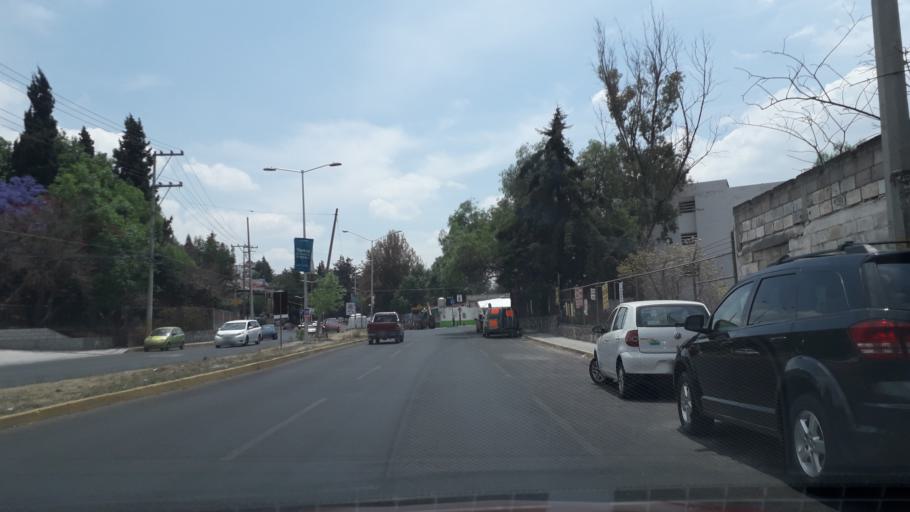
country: MX
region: Puebla
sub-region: Puebla
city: Galaxia la Calera
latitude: 19.0077
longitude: -98.1802
